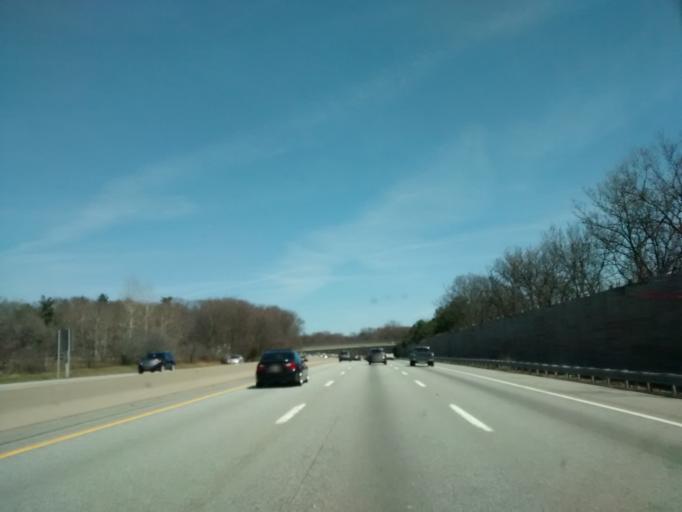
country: US
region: Massachusetts
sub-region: Middlesex County
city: Framingham Center
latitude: 42.3013
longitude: -71.4587
